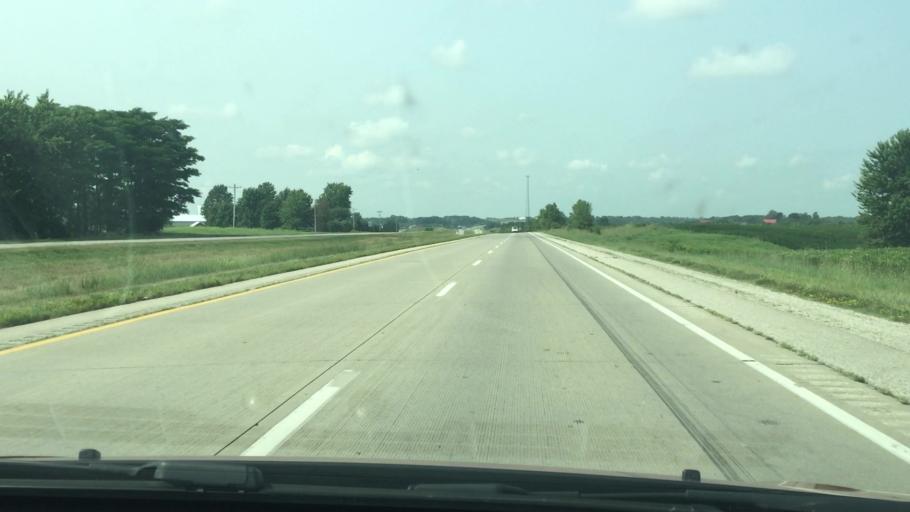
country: US
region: Iowa
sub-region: Cedar County
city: Durant
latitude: 41.5132
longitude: -90.9128
